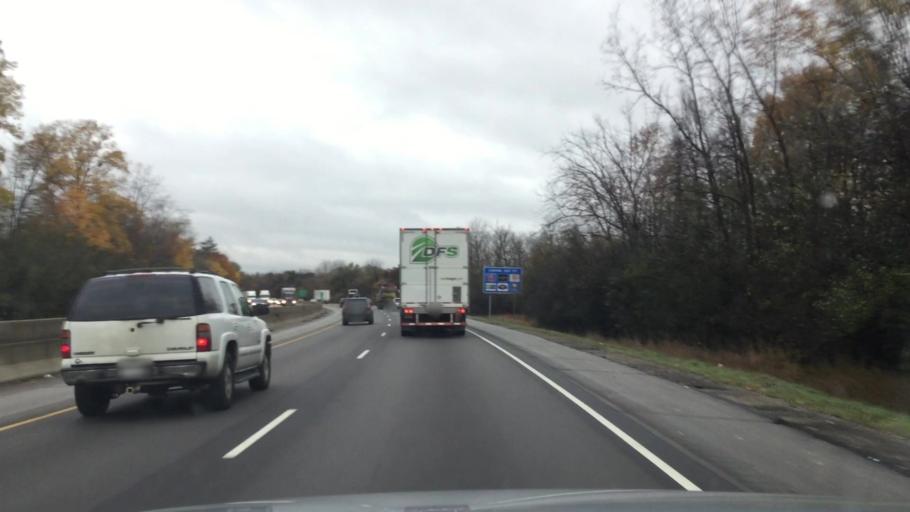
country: US
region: Michigan
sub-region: Washtenaw County
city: Ann Arbor
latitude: 42.2370
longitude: -83.7103
